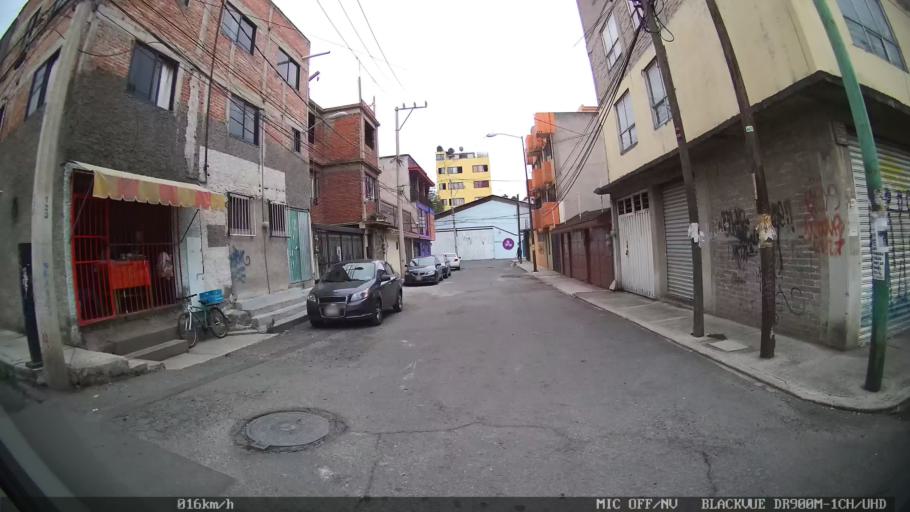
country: MX
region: Mexico City
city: Tlalpan
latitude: 19.3063
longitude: -99.1609
